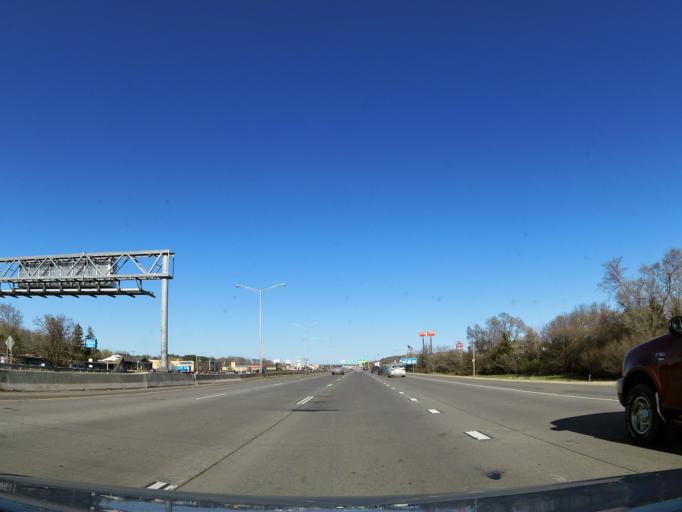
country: US
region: Wisconsin
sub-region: Saint Croix County
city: Hudson
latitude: 44.9627
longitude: -92.7394
